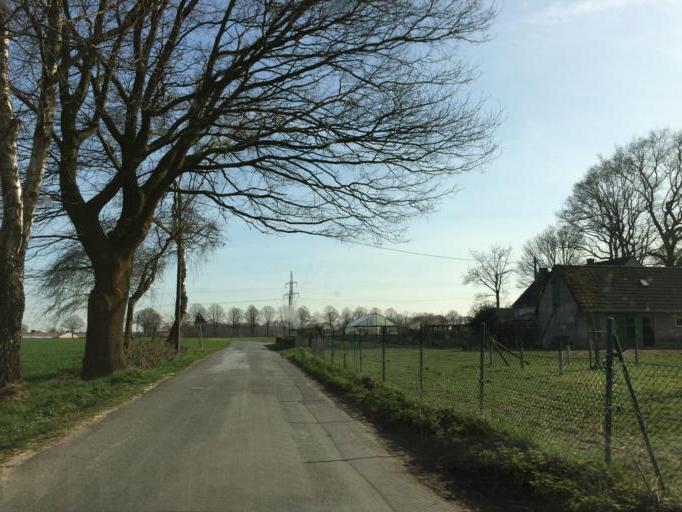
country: DE
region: North Rhine-Westphalia
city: Marl
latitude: 51.6934
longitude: 7.0374
